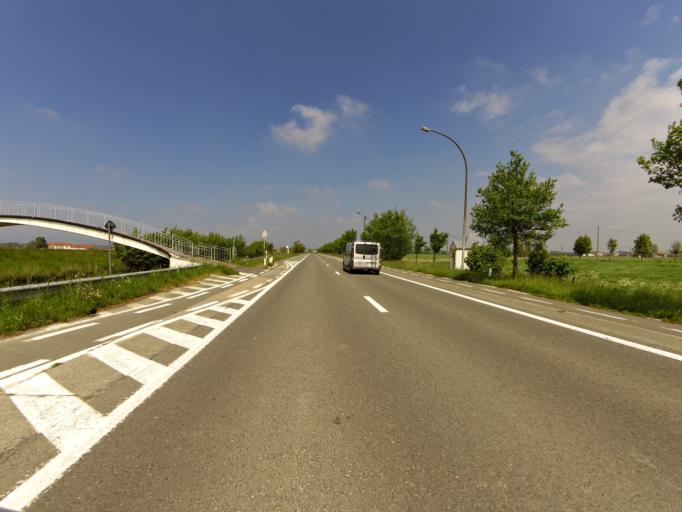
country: BE
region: Flanders
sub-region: Provincie West-Vlaanderen
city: Veurne
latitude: 51.0878
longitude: 2.6746
